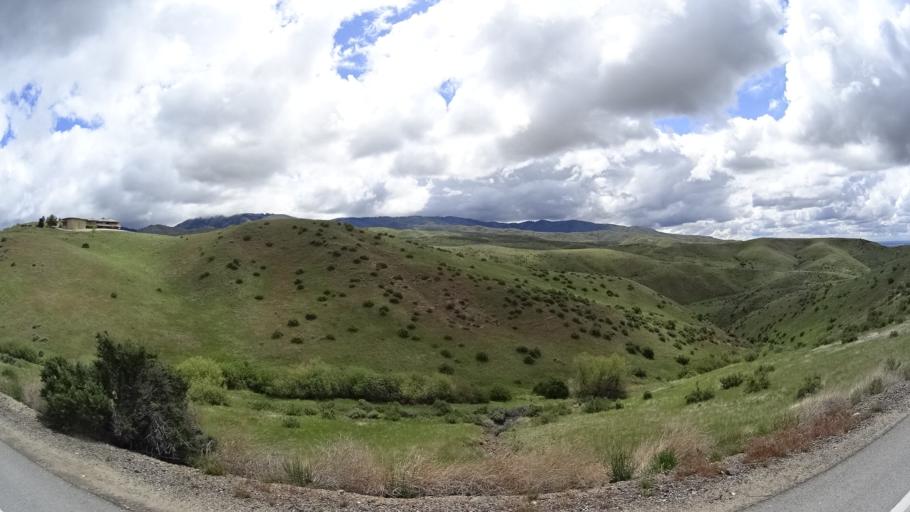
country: US
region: Idaho
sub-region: Ada County
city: Boise
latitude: 43.6950
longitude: -116.1710
